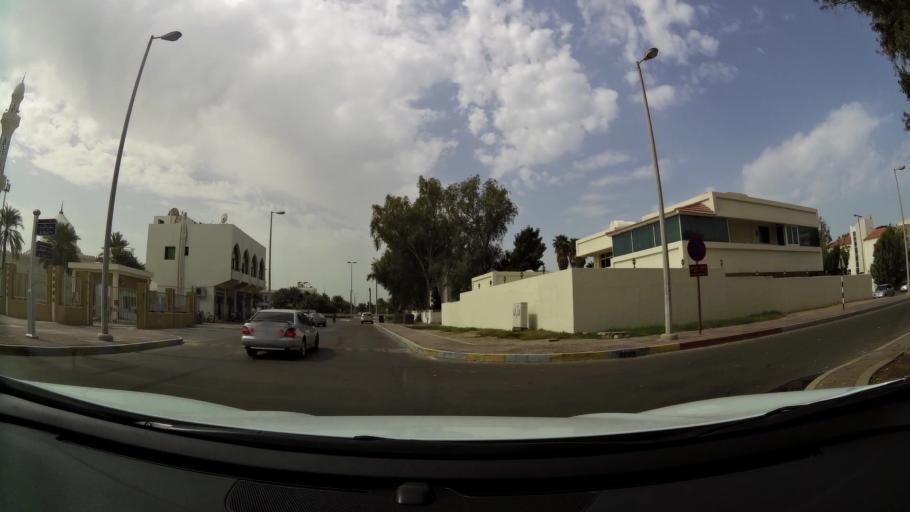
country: AE
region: Abu Dhabi
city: Abu Dhabi
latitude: 24.4521
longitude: 54.3559
